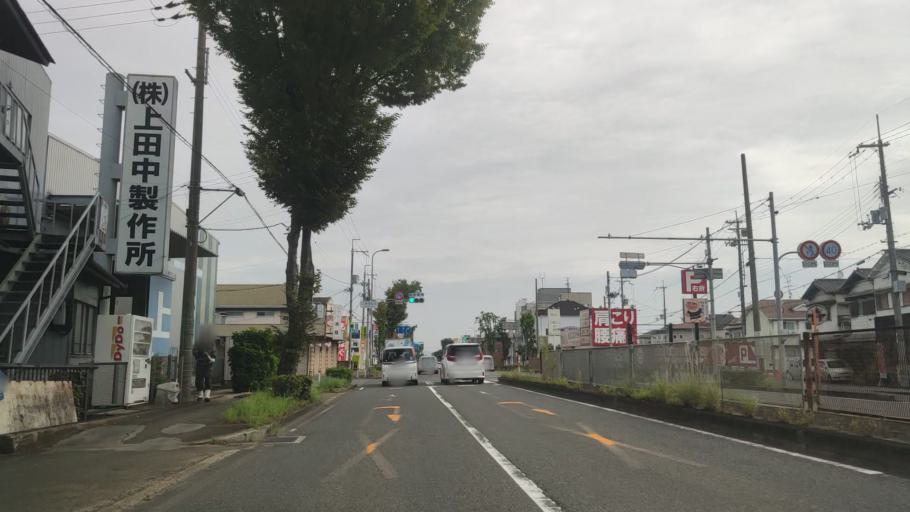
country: JP
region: Osaka
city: Tondabayashicho
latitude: 34.4489
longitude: 135.5570
